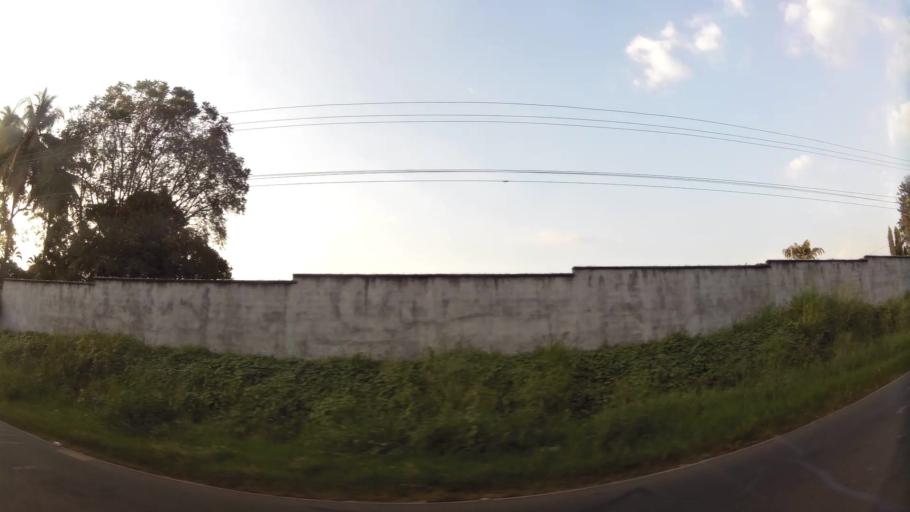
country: GT
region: Retalhuleu
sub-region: Municipio de Retalhuleu
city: Retalhuleu
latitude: 14.5488
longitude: -91.6620
